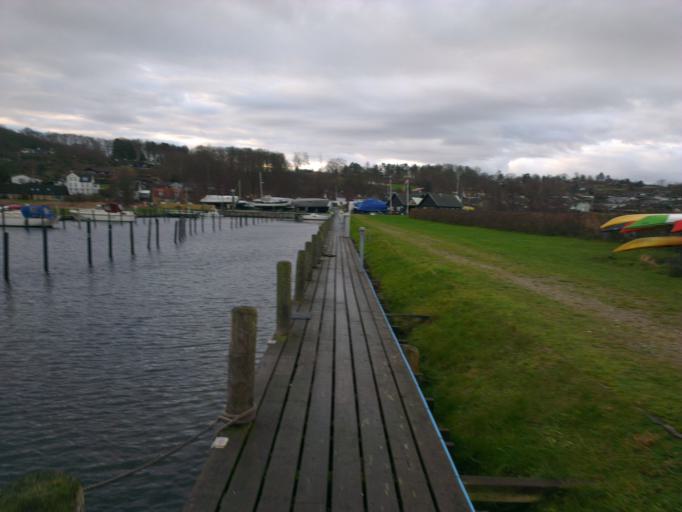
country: DK
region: Capital Region
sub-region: Frederikssund Kommune
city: Jaegerspris
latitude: 55.8574
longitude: 12.0091
